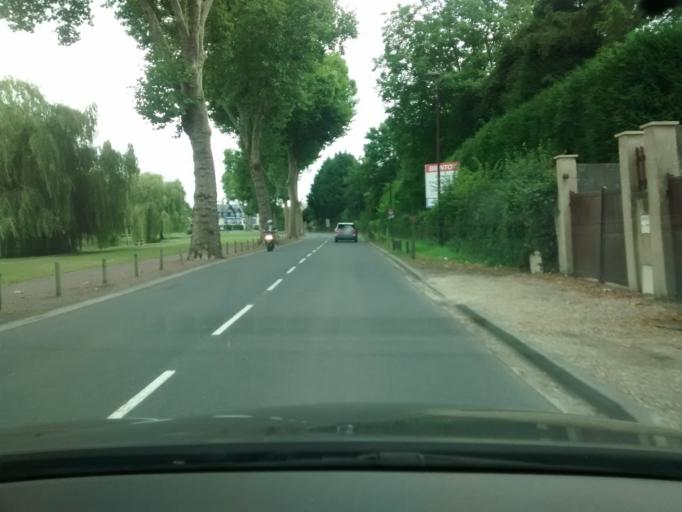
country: FR
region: Lower Normandy
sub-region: Departement du Calvados
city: Touques
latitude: 49.3414
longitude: 0.0898
